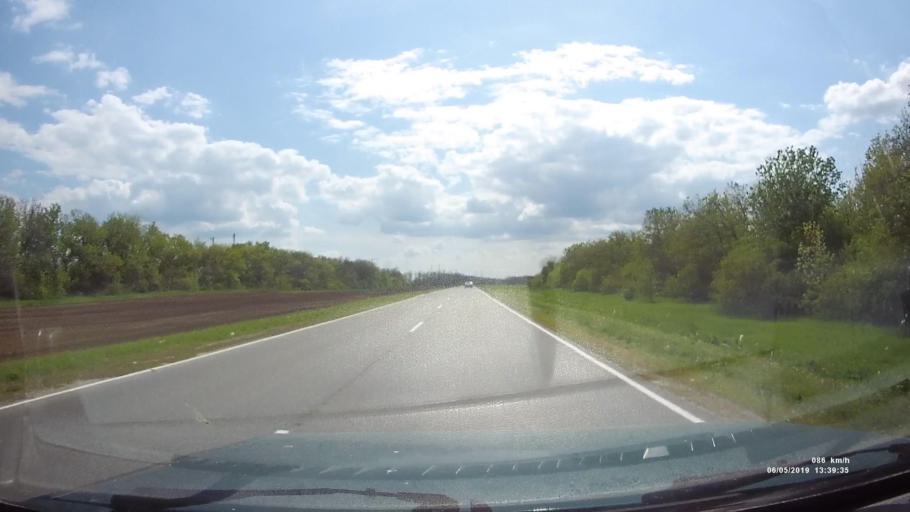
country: RU
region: Rostov
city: Ust'-Donetskiy
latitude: 47.6740
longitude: 40.7016
